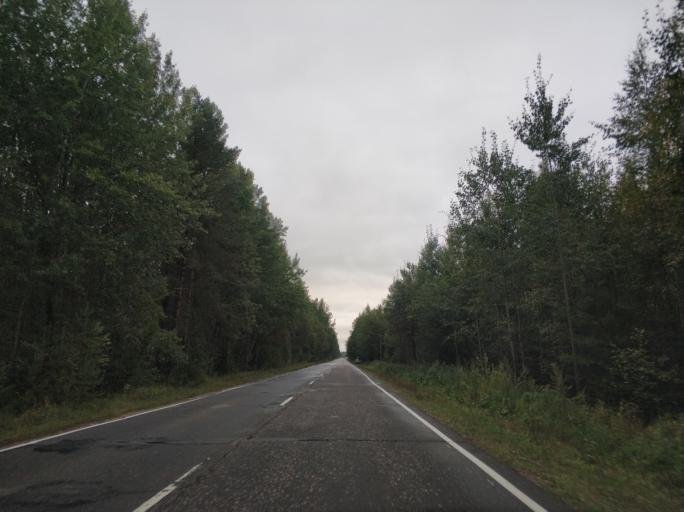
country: RU
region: Leningrad
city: Borisova Griva
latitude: 60.1717
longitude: 30.9199
